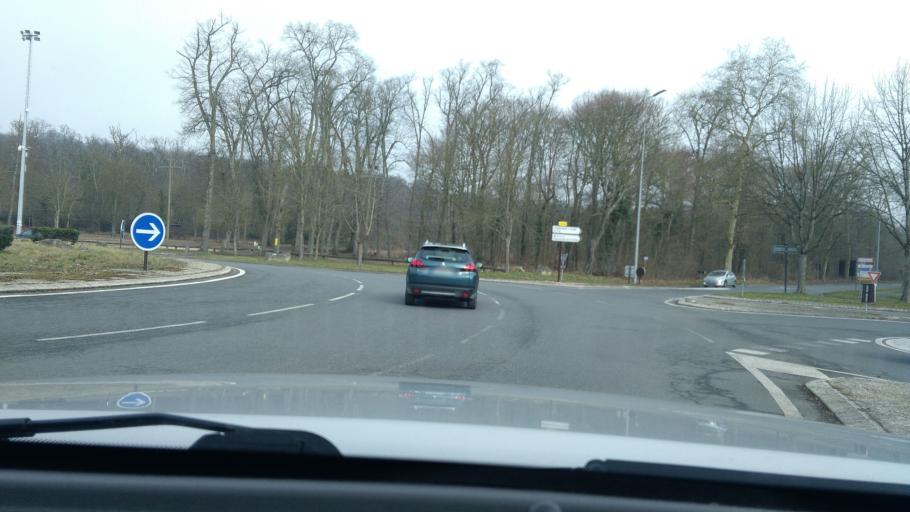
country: FR
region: Ile-de-France
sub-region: Departement de Seine-et-Marne
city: Fontainebleau
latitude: 48.4082
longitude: 2.6867
